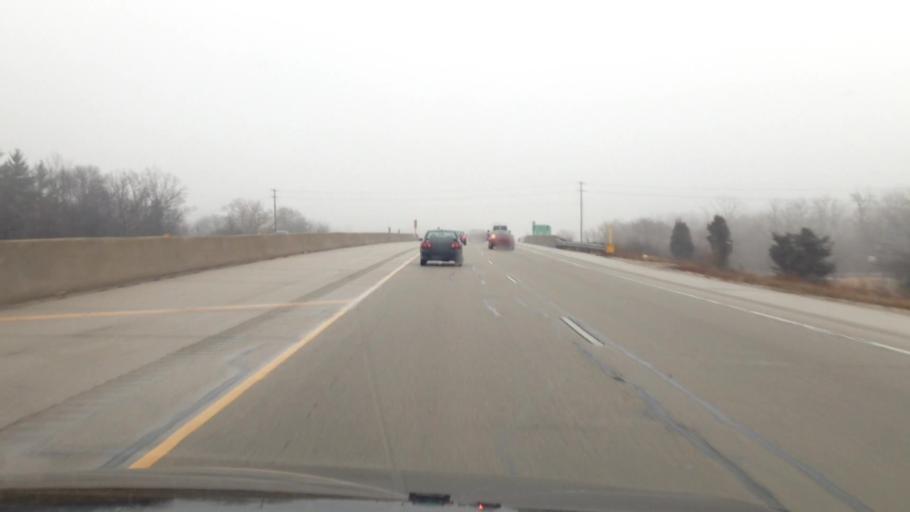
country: US
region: Wisconsin
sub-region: Waukesha County
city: Muskego
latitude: 42.9366
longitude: -88.1488
